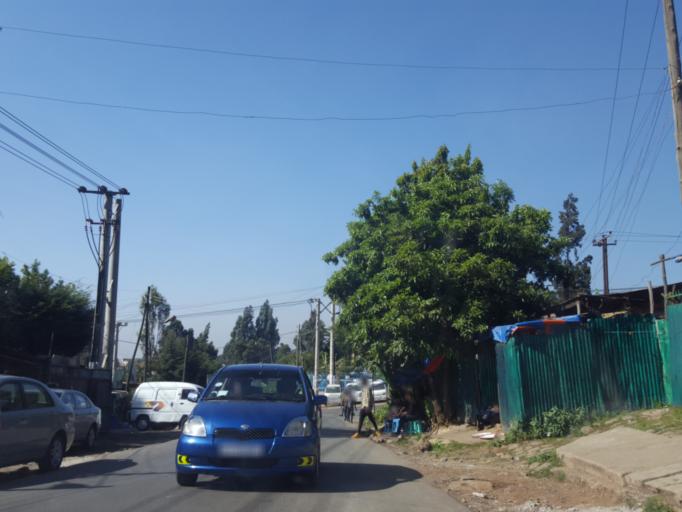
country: ET
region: Adis Abeba
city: Addis Ababa
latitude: 9.0513
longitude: 38.7378
